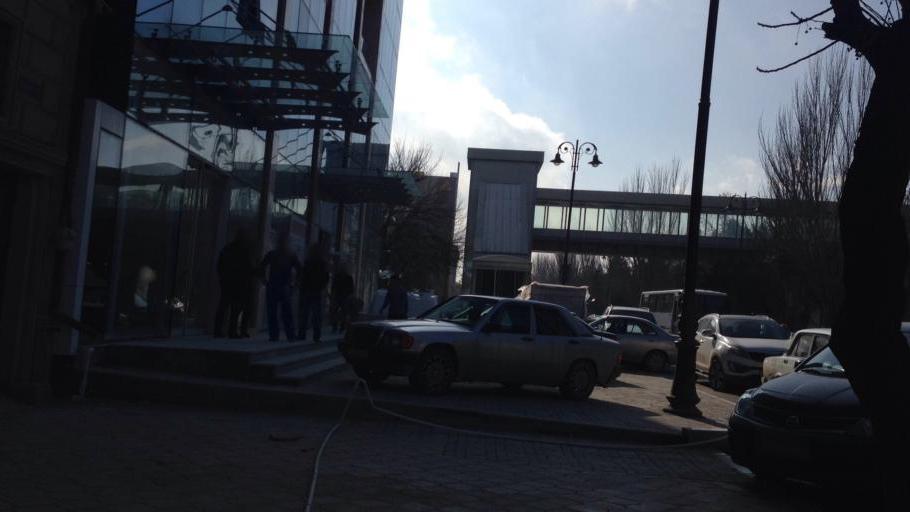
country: AZ
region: Baki
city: Bilajari
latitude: 40.4127
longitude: 49.8469
